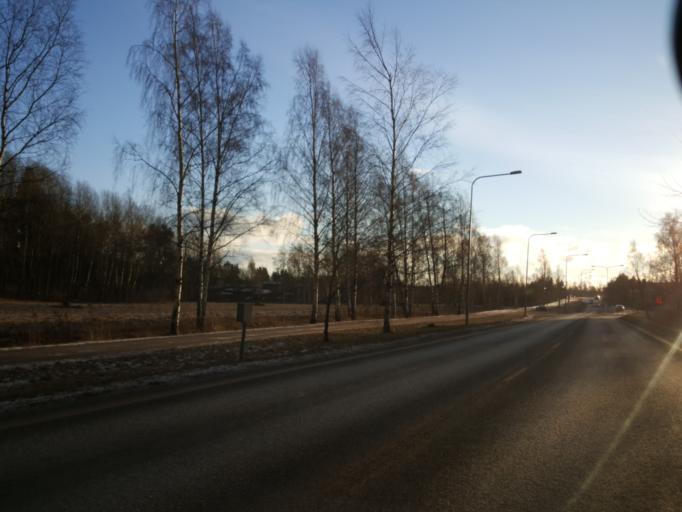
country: FI
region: Uusimaa
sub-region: Helsinki
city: Vantaa
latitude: 60.2449
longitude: 24.9775
